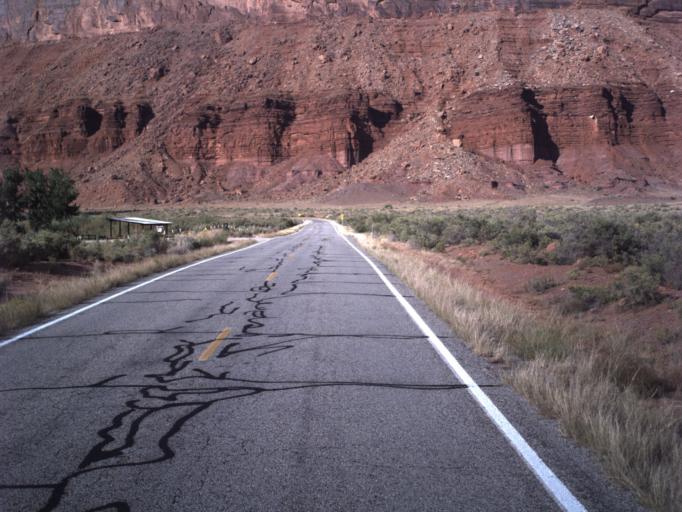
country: US
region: Utah
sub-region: Grand County
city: Moab
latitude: 38.7606
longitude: -109.3228
